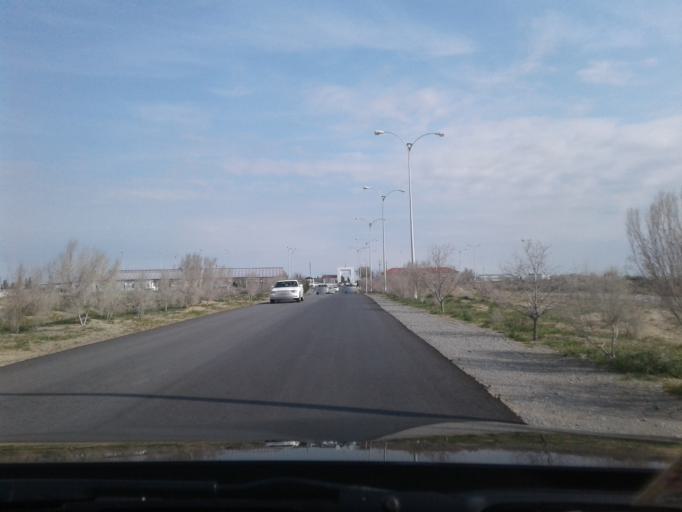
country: TM
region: Ahal
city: Ashgabat
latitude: 38.0947
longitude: 58.3846
